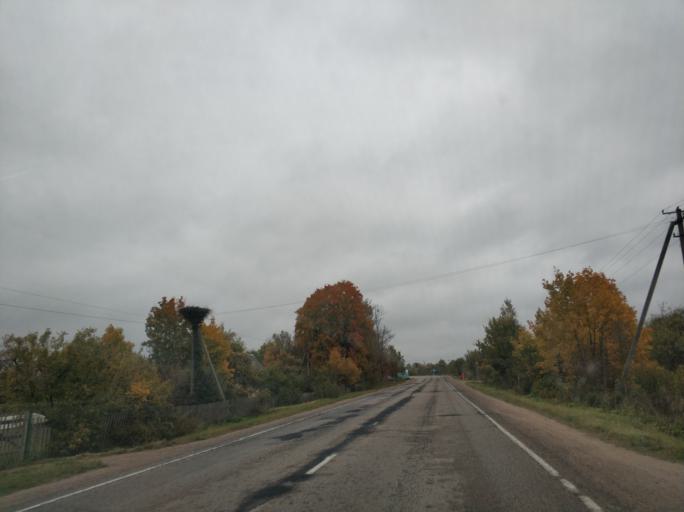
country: BY
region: Vitebsk
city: Rasony
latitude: 56.0541
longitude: 28.7115
